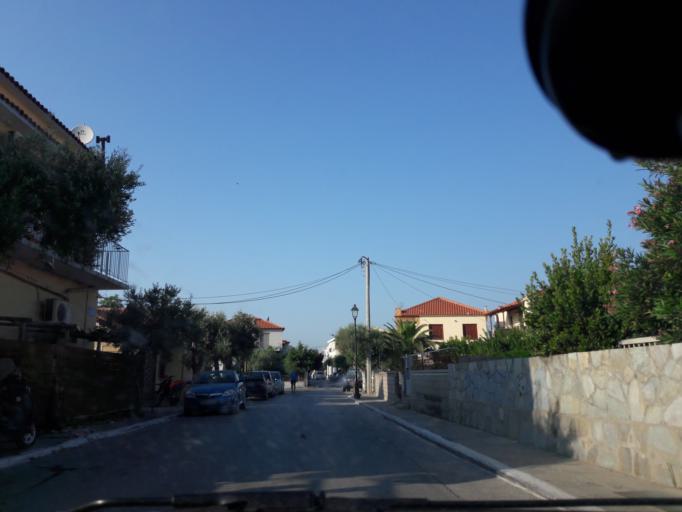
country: GR
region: North Aegean
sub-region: Nomos Lesvou
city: Myrina
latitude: 39.8718
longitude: 25.0612
